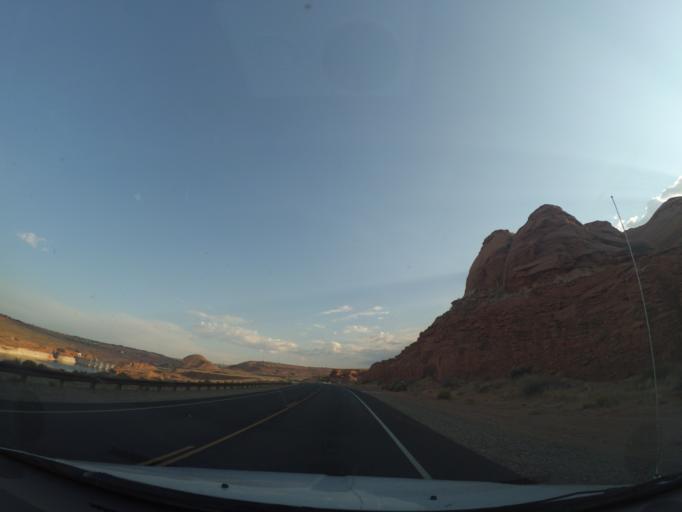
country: US
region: Arizona
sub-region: Coconino County
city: Page
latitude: 36.9494
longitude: -111.4937
